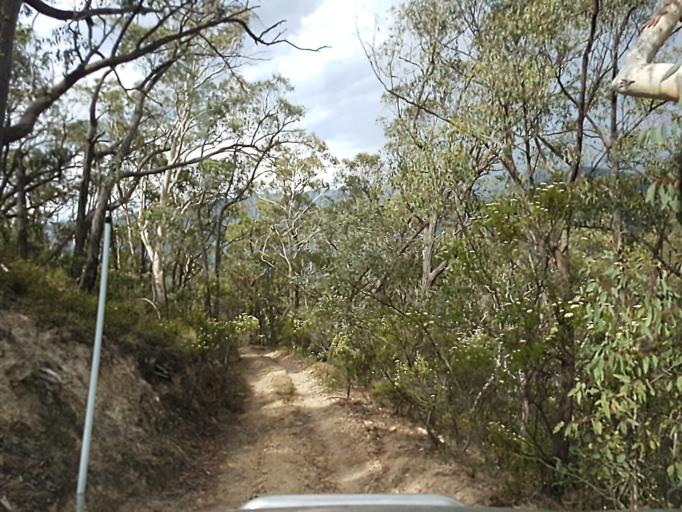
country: AU
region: New South Wales
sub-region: Snowy River
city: Jindabyne
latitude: -36.8792
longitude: 148.2164
